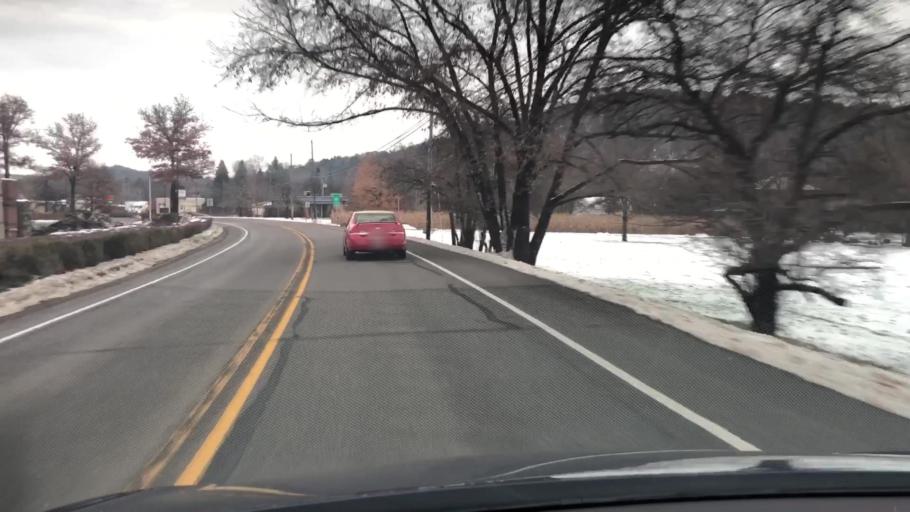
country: US
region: Pennsylvania
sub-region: Jefferson County
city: Brookville
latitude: 41.1188
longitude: -79.1890
